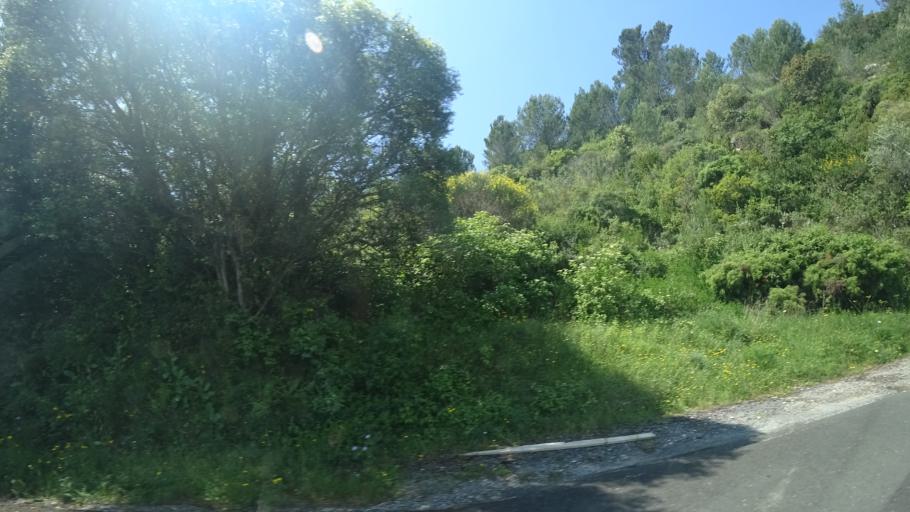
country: FR
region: Languedoc-Roussillon
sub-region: Departement de l'Herault
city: Olonzac
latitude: 43.3480
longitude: 2.7505
